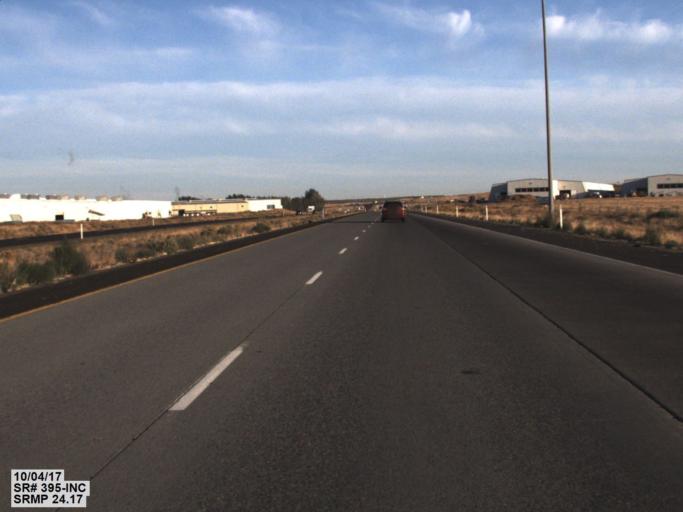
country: US
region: Washington
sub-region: Franklin County
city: Pasco
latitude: 46.2718
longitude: -119.0889
